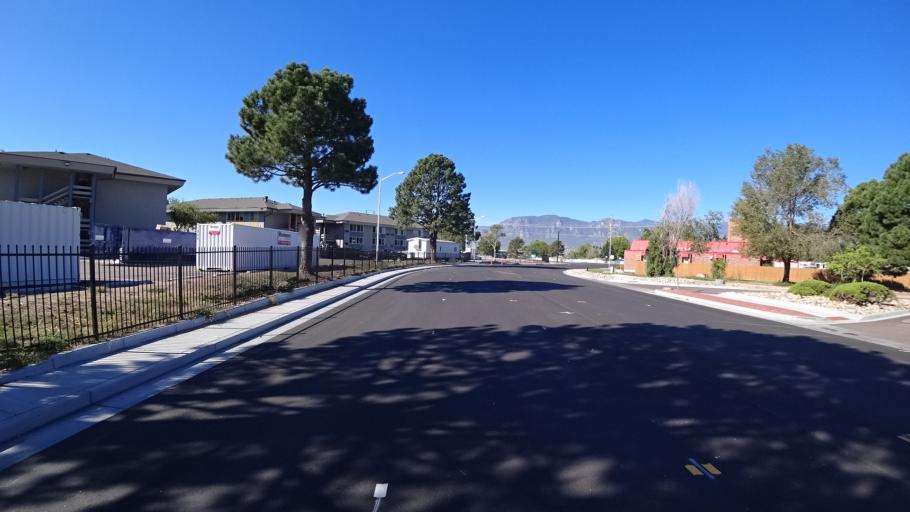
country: US
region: Colorado
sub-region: El Paso County
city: Stratmoor
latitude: 38.7846
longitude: -104.7561
